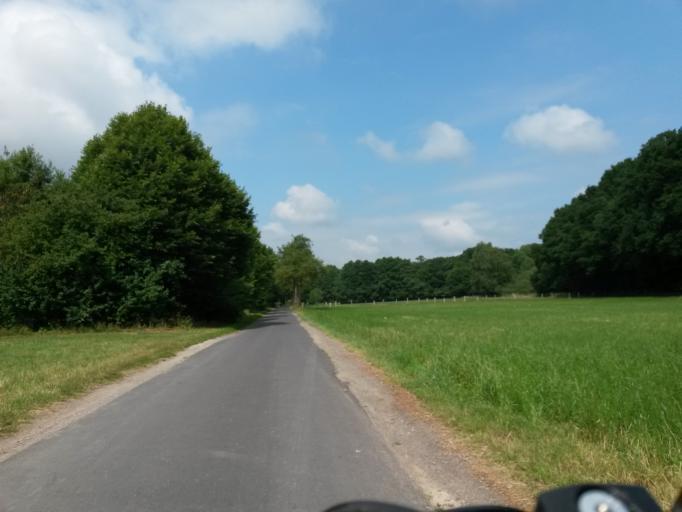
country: DE
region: North Rhine-Westphalia
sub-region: Regierungsbezirk Dusseldorf
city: Nettetal
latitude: 51.3387
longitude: 6.2583
